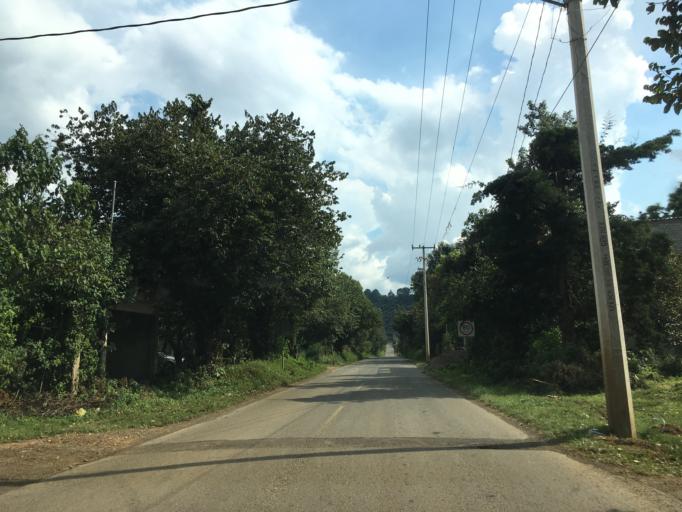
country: MX
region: Michoacan
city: Tingambato
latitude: 19.4942
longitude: -101.8554
